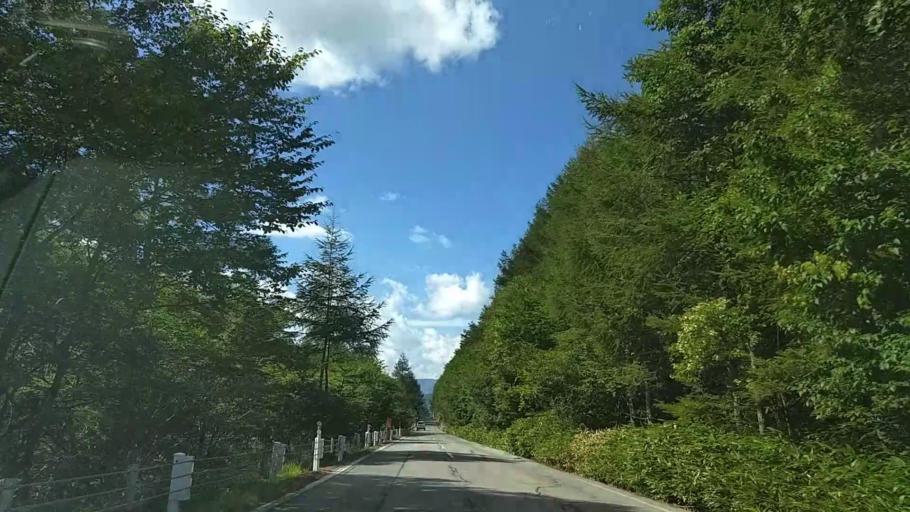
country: JP
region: Nagano
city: Chino
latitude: 36.0898
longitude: 138.2770
